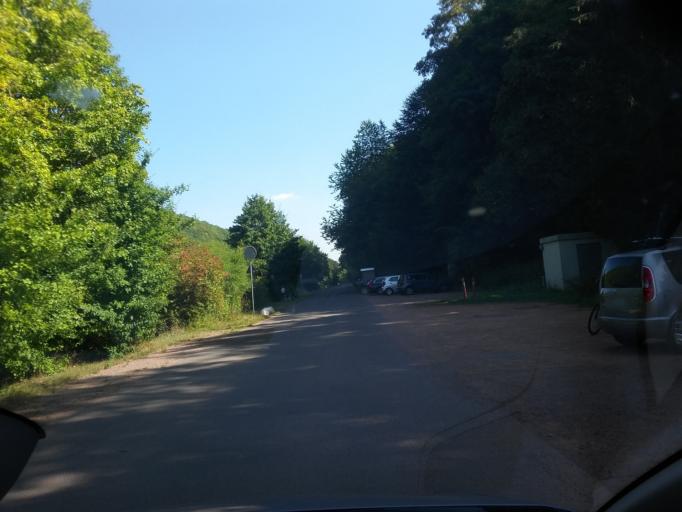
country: DE
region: Saarland
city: Orscholz
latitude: 49.4955
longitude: 6.5505
